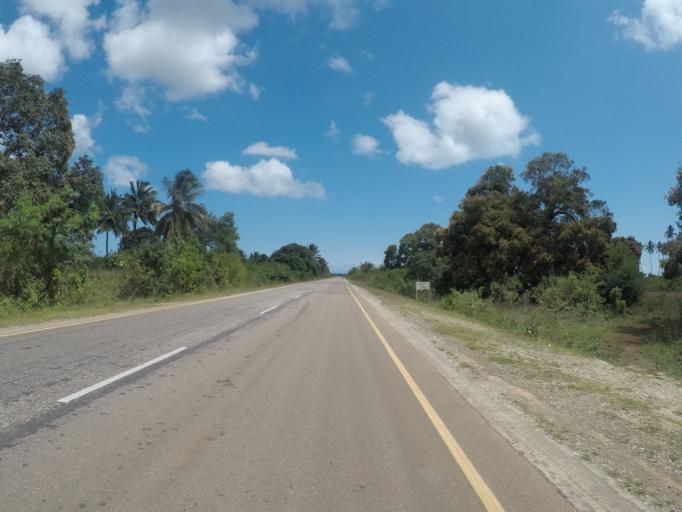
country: TZ
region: Zanzibar Central/South
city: Koani
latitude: -6.2437
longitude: 39.3563
